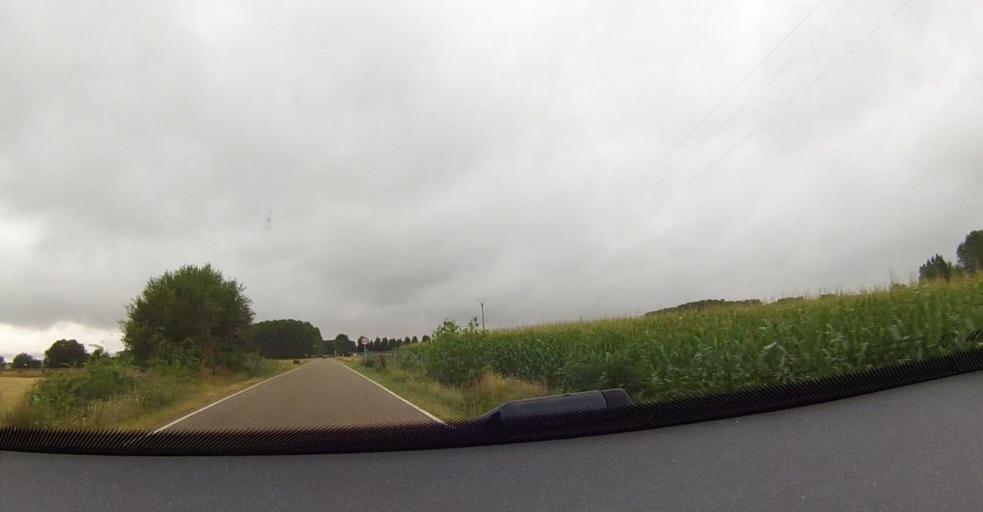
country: ES
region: Castille and Leon
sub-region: Provincia de Palencia
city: Pedrosa de la Vega
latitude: 42.4796
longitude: -4.7311
